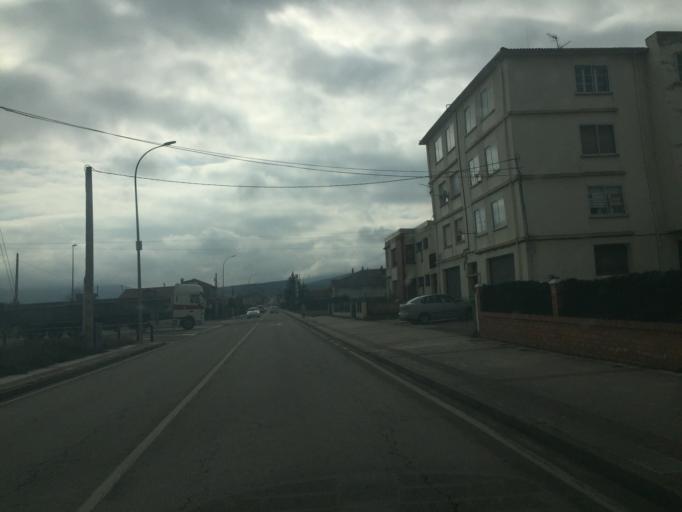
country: ES
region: Castille and Leon
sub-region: Provincia de Burgos
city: Medina de Pomar
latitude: 42.9315
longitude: -3.5754
